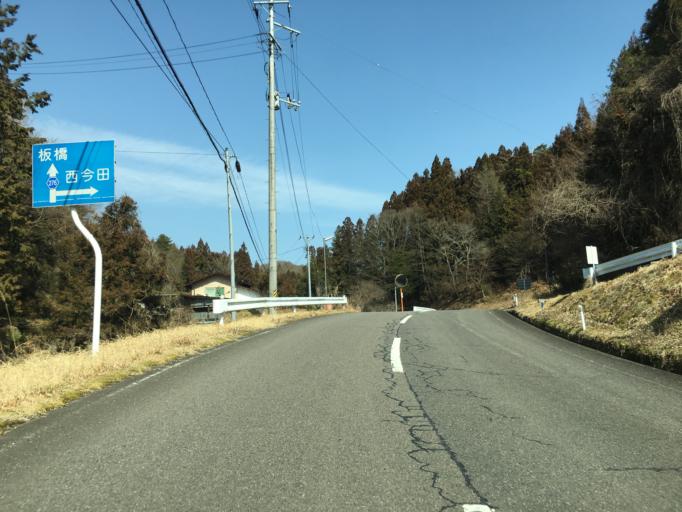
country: JP
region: Fukushima
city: Ishikawa
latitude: 37.0974
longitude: 140.4522
